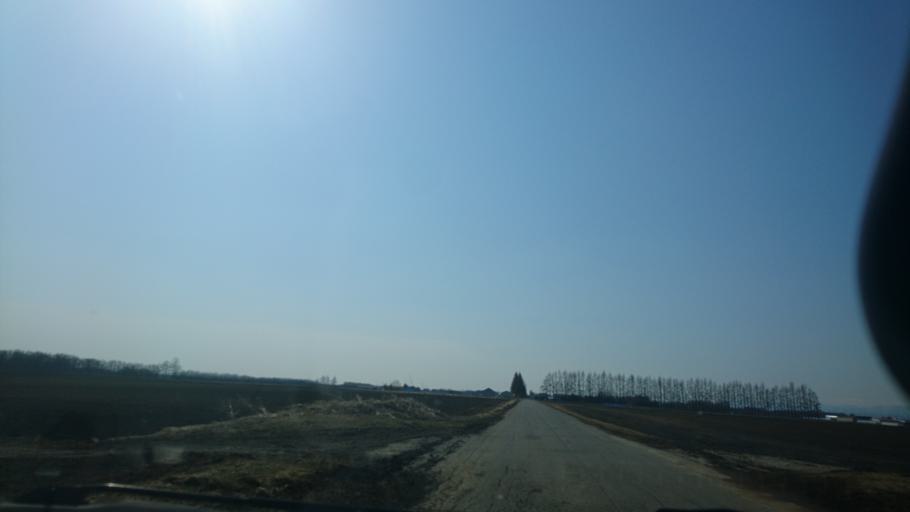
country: JP
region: Hokkaido
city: Obihiro
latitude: 42.9115
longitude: 143.0907
